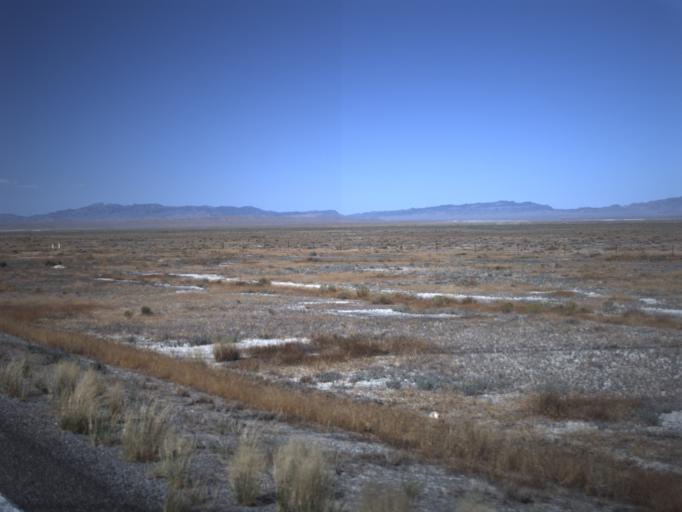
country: US
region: Utah
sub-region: Millard County
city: Delta
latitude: 39.2455
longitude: -112.9058
